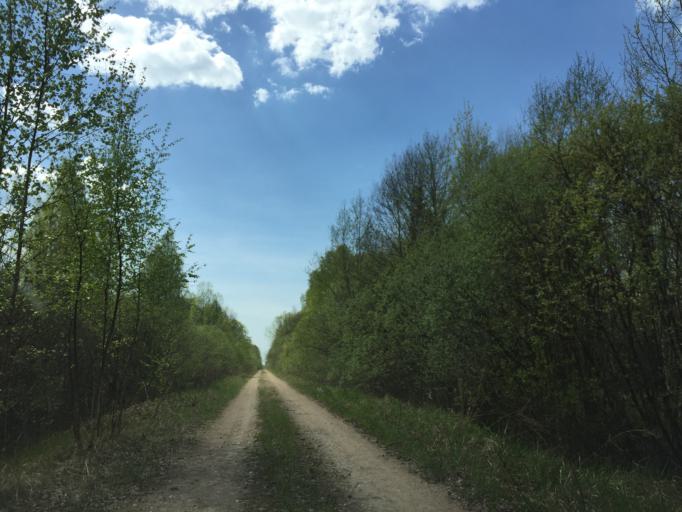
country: LV
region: Limbazu Rajons
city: Limbazi
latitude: 57.3920
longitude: 24.5699
